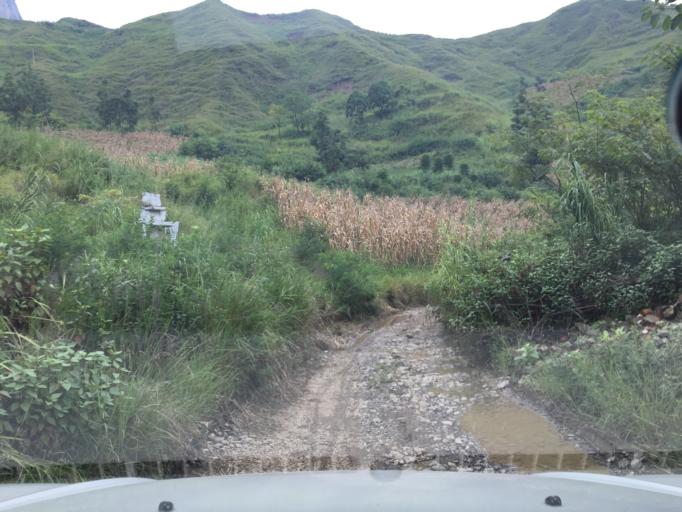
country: CN
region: Guizhou Sheng
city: Liupanshui
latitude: 26.0378
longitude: 105.1887
